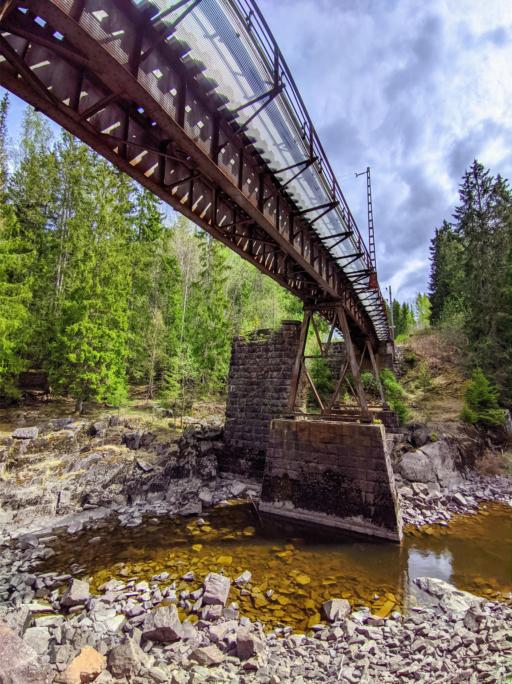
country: NO
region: Ostfold
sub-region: Spydeberg
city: Spydeberg
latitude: 59.6078
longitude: 11.1181
